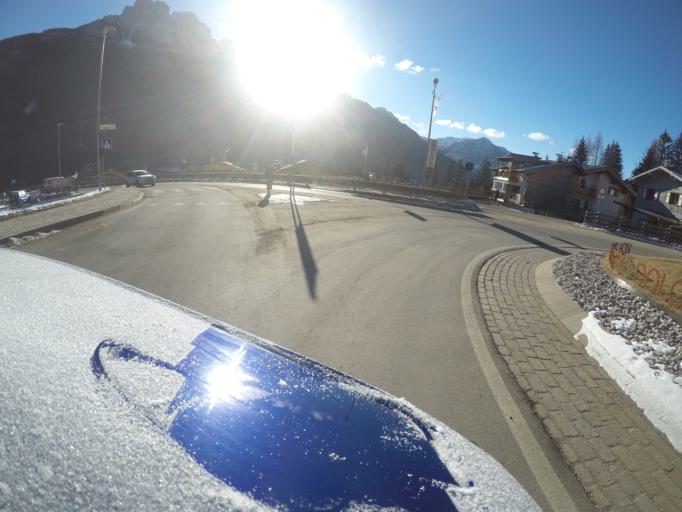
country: IT
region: Trentino-Alto Adige
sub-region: Provincia di Trento
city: Vigo di Fassa
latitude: 46.4180
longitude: 11.6747
